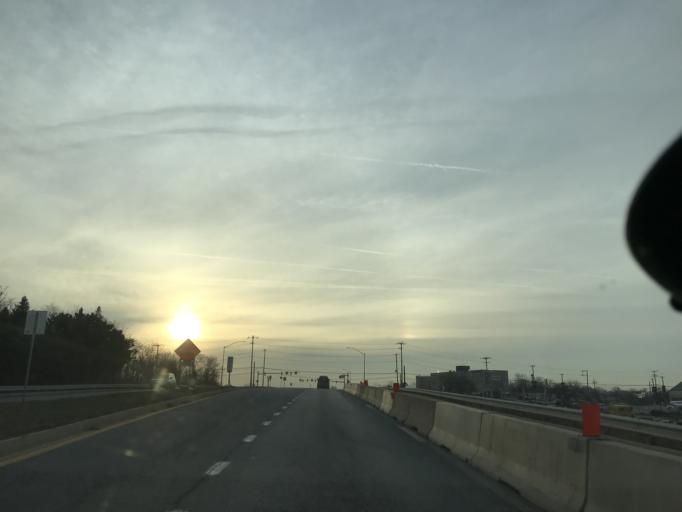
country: US
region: Maryland
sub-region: Prince George's County
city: Woodlawn
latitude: 38.9532
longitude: -76.8871
